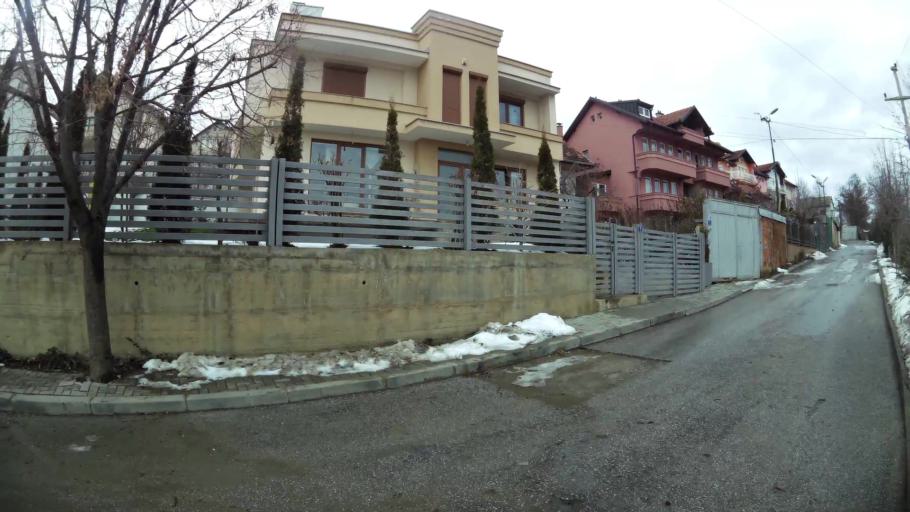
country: XK
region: Pristina
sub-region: Komuna e Prishtines
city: Pristina
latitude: 42.6815
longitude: 21.1727
